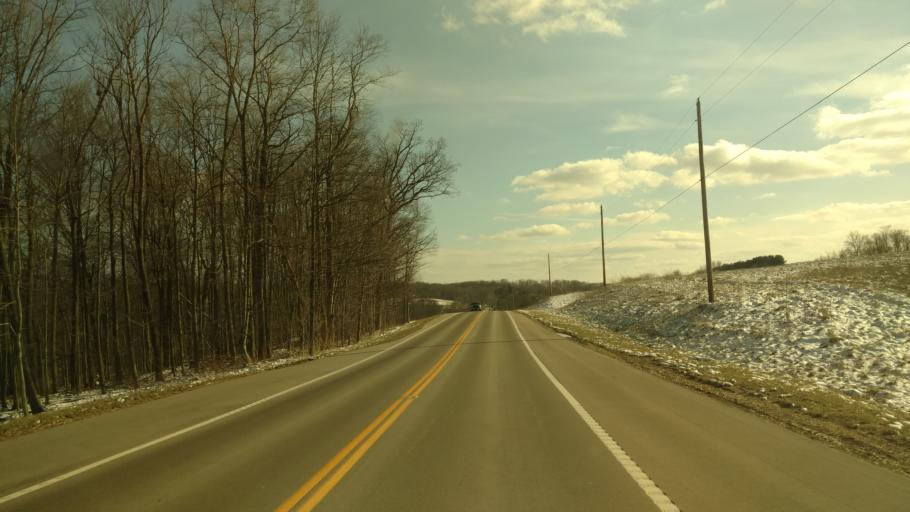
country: US
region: Ohio
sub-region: Ashland County
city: Loudonville
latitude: 40.7171
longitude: -82.2408
